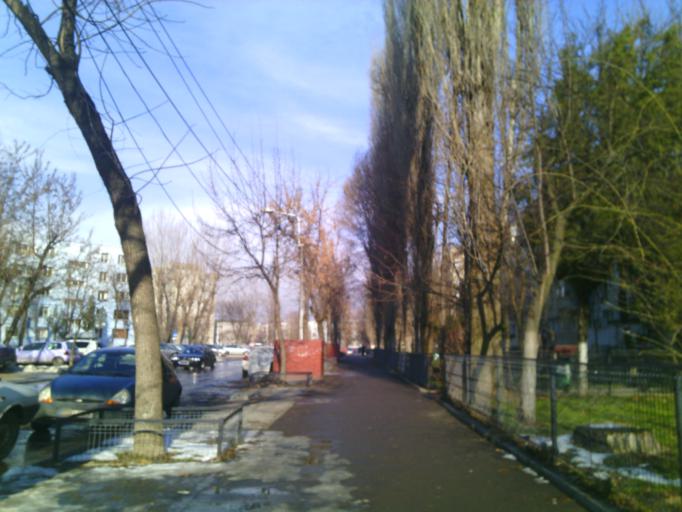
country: RO
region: Bucuresti
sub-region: Municipiul Bucuresti
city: Bucuresti
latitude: 44.3815
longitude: 26.1033
